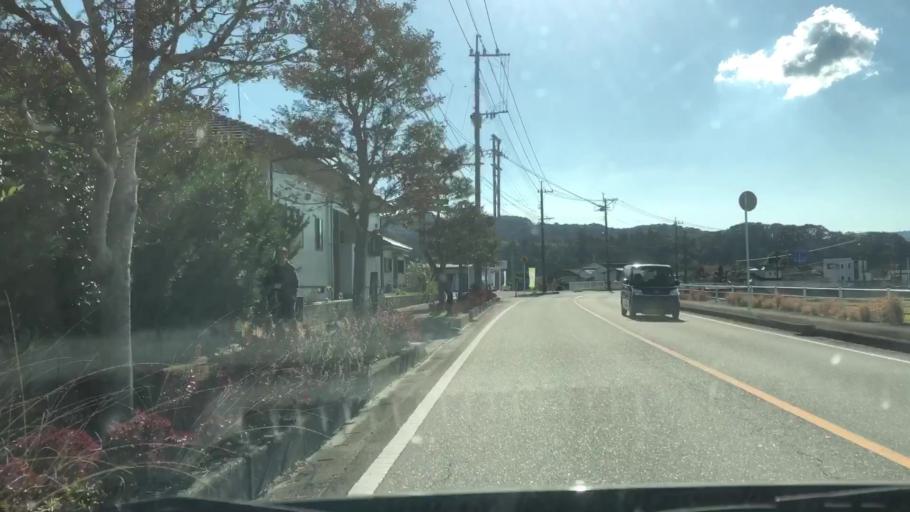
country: JP
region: Kagoshima
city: Satsumasendai
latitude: 31.8580
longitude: 130.3915
